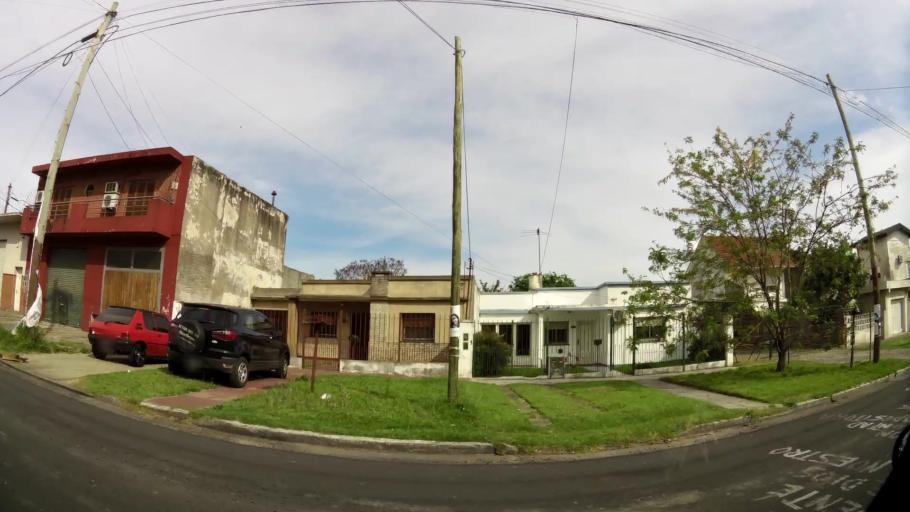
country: AR
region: Buenos Aires
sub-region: Partido de Quilmes
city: Quilmes
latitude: -34.7460
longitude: -58.2775
